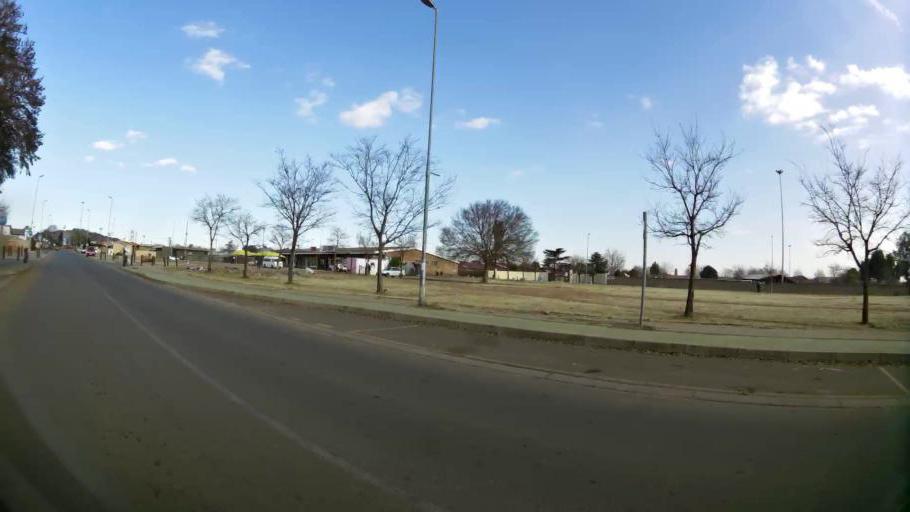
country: ZA
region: Gauteng
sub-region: City of Johannesburg Metropolitan Municipality
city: Soweto
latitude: -26.2538
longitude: 27.9081
